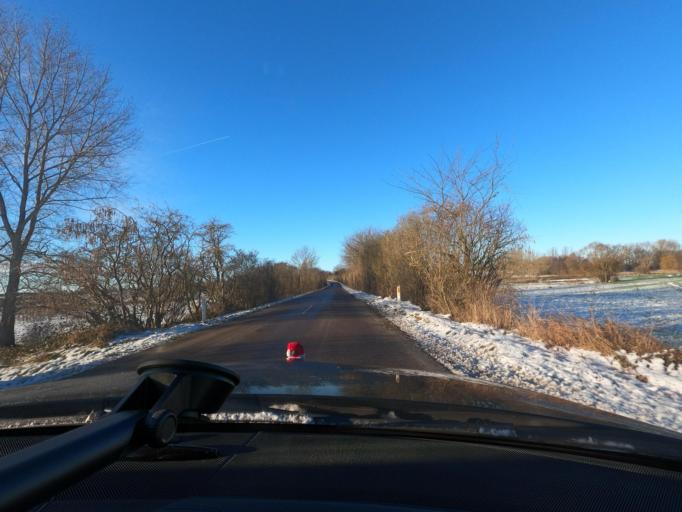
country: DK
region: South Denmark
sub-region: Sonderborg Kommune
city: Horuphav
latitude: 54.8775
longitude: 9.9165
